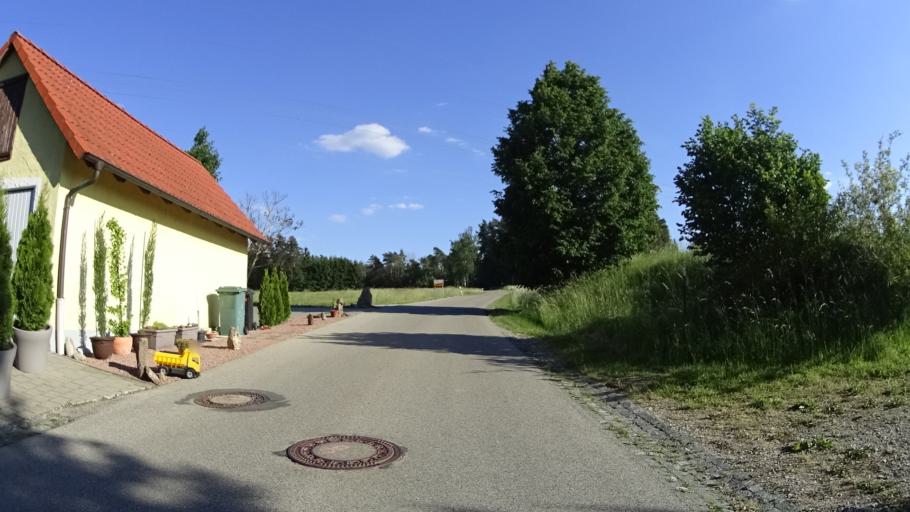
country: DE
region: Bavaria
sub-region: Regierungsbezirk Mittelfranken
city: Lichtenau
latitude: 49.1591
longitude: 10.3793
